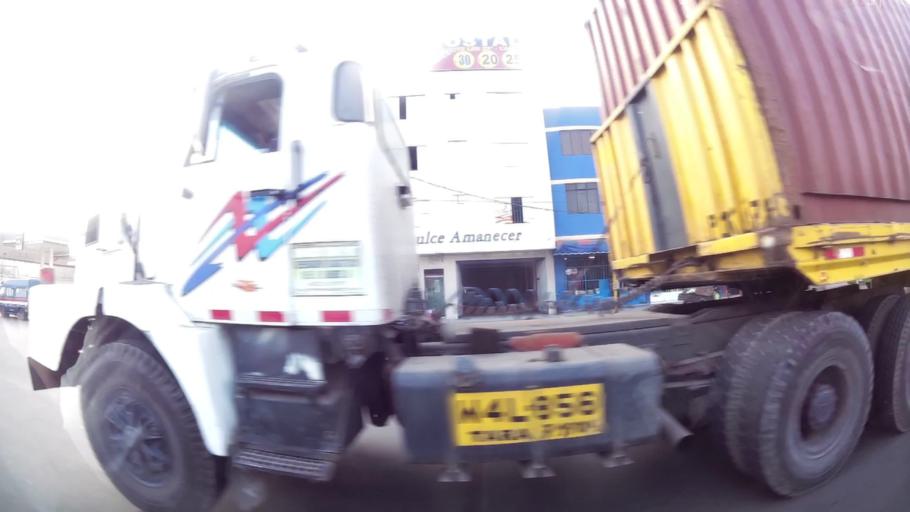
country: PE
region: Lima
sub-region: Lima
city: Independencia
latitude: -11.9905
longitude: -77.1072
